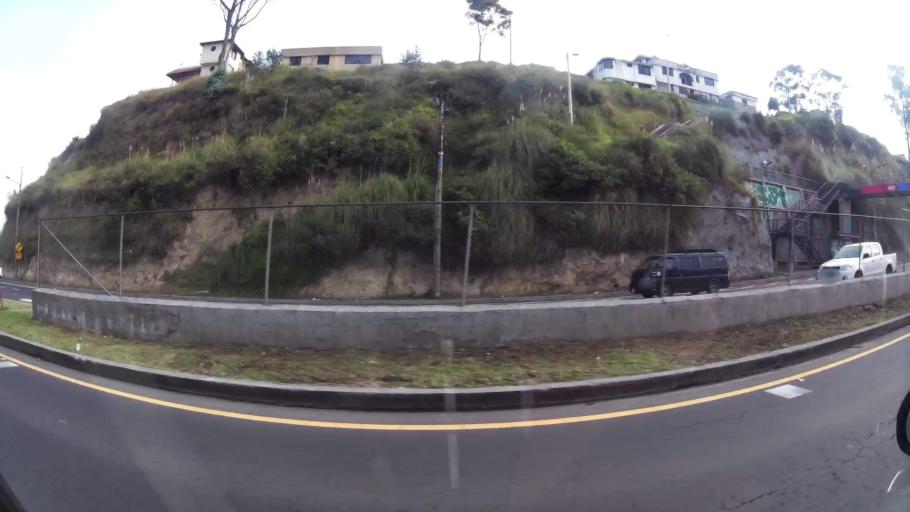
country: EC
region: Pichincha
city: Quito
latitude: -0.2345
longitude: -78.4908
